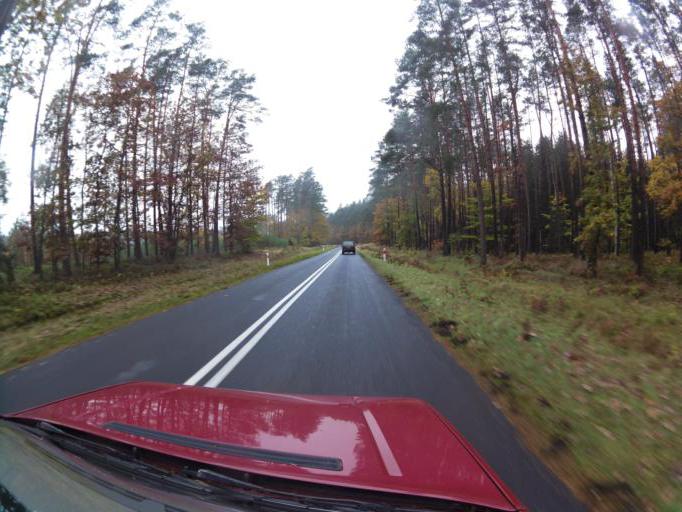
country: PL
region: West Pomeranian Voivodeship
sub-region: Powiat policki
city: Dobra
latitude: 53.5818
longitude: 14.4210
